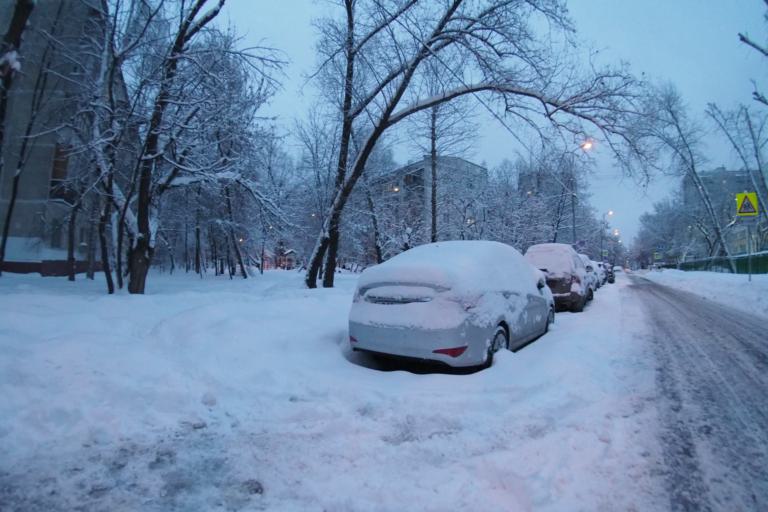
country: RU
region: Moscow
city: Perovo
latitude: 55.7465
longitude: 37.7839
